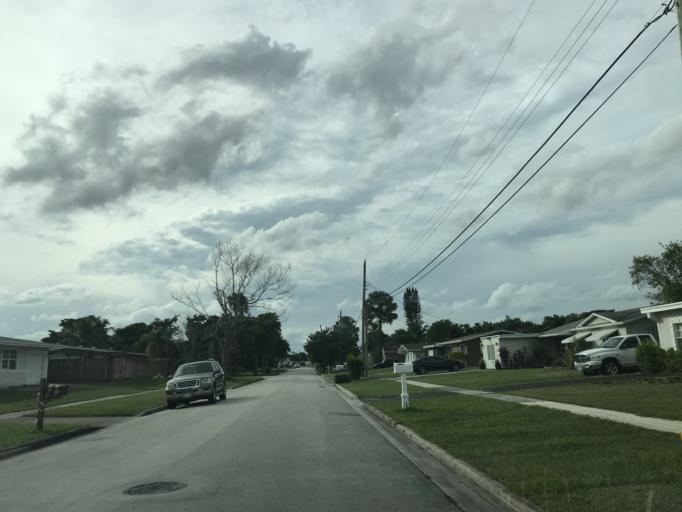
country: US
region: Florida
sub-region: Broward County
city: Margate
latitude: 26.2567
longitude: -80.2055
